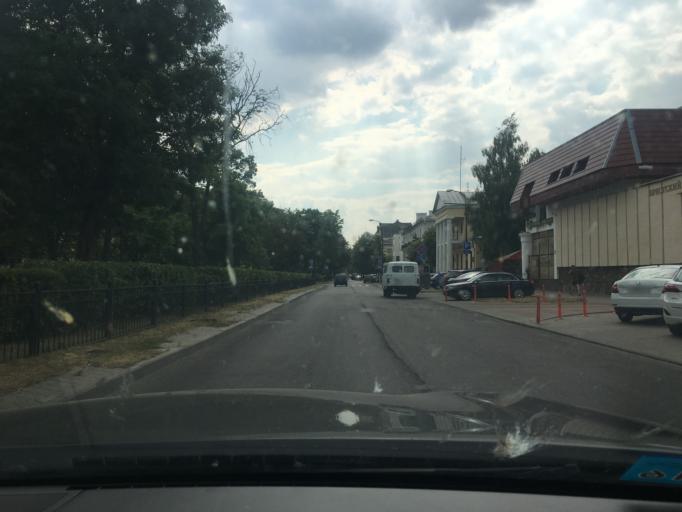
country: BY
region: Brest
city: Brest
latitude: 52.0976
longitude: 23.6876
